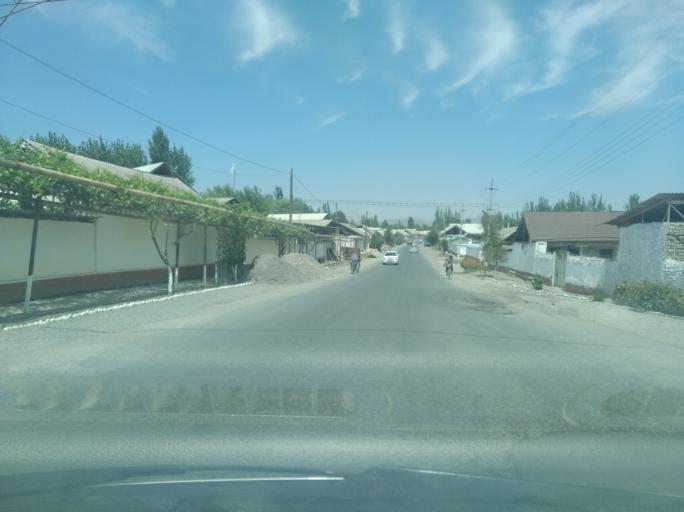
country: KG
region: Osh
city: Aravan
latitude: 40.6209
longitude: 72.4523
